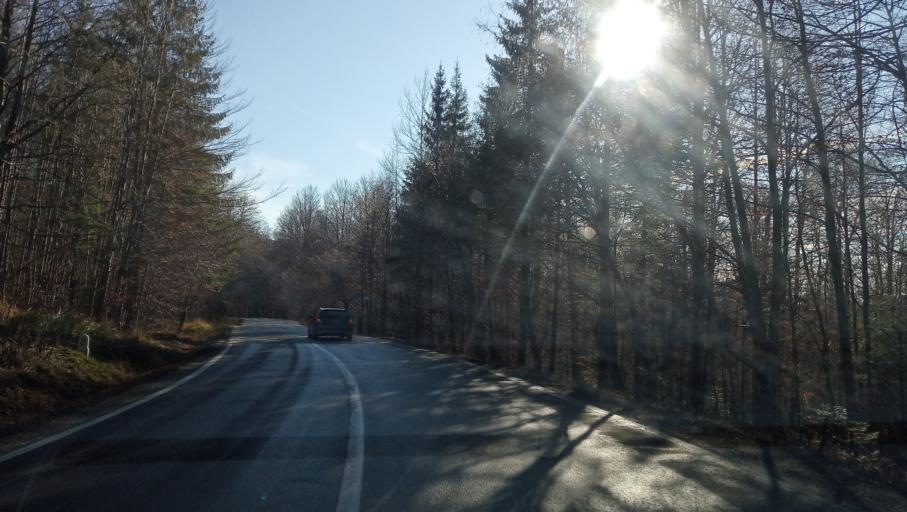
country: RO
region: Brasov
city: Crivina
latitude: 45.4653
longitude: 25.9409
